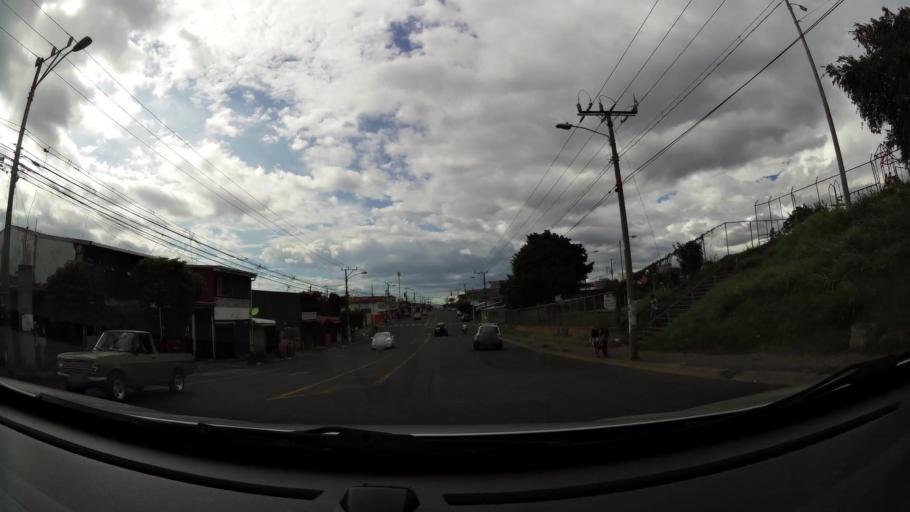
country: CR
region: Heredia
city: La Asuncion
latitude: 9.9561
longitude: -84.1556
